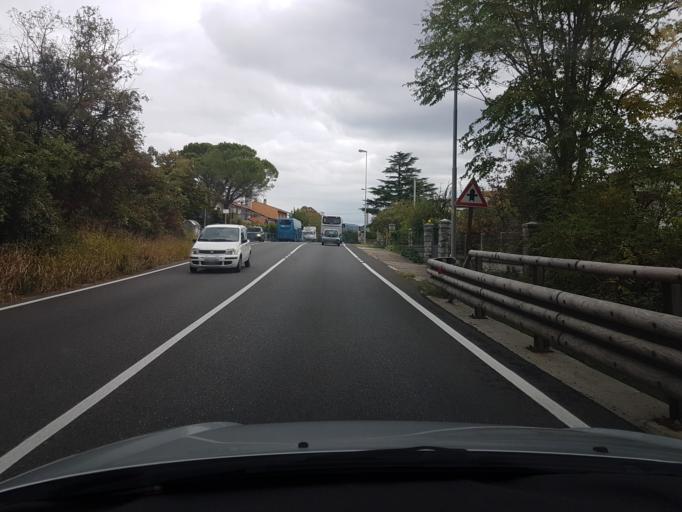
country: IT
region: Friuli Venezia Giulia
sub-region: Provincia di Trieste
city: Sistiana-Visogliano
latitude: 45.7731
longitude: 13.6230
